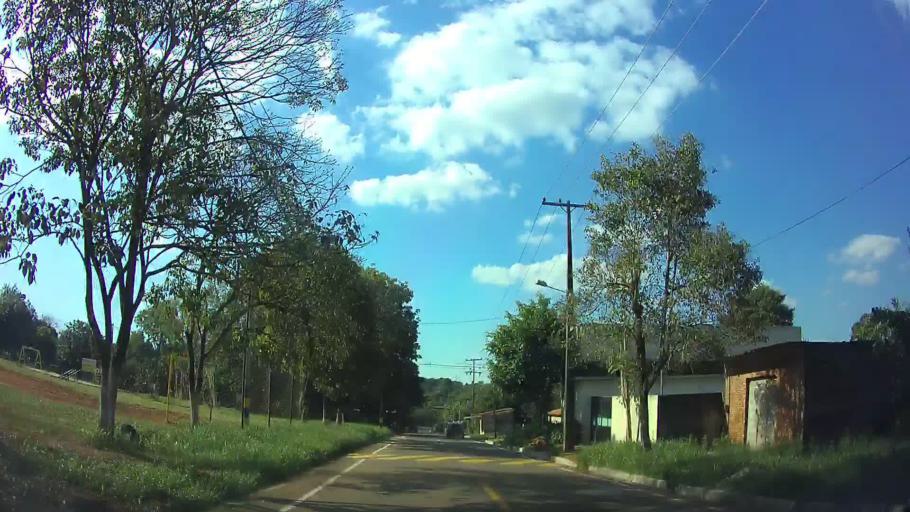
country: PY
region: Central
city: San Lorenzo
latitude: -25.2737
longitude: -57.4636
